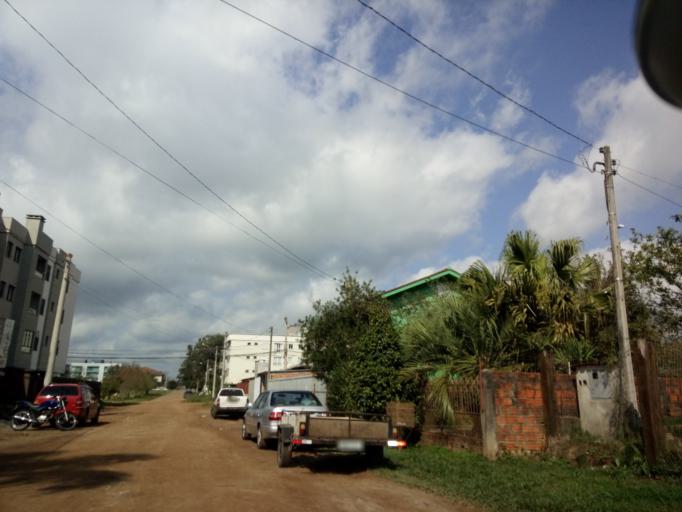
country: BR
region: Rio Grande do Sul
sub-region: Santa Maria
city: Santa Maria
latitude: -29.7033
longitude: -53.7205
